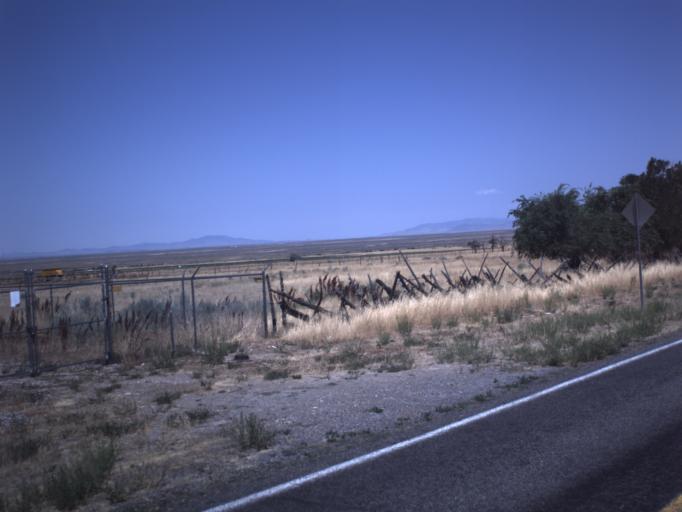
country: US
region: Utah
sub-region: Millard County
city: Delta
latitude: 39.3826
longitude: -112.3360
